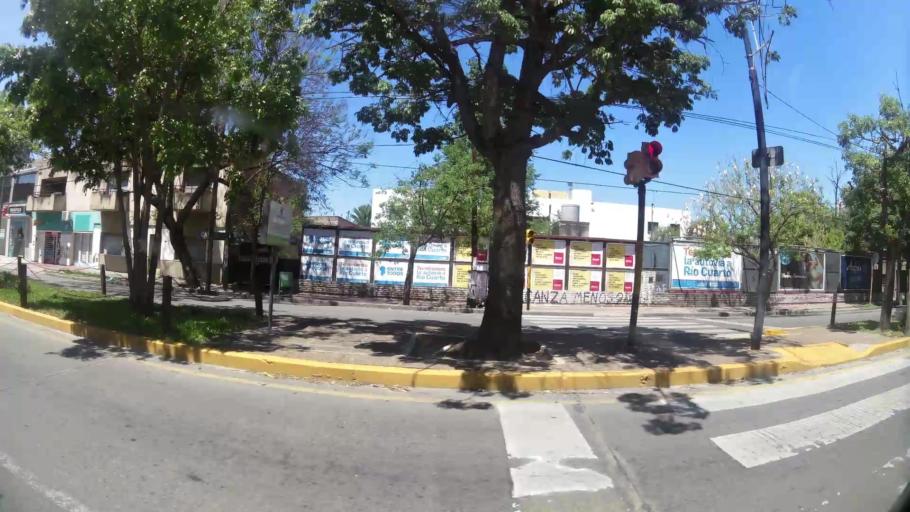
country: AR
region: Cordoba
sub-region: Departamento de Capital
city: Cordoba
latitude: -31.4130
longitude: -64.2047
